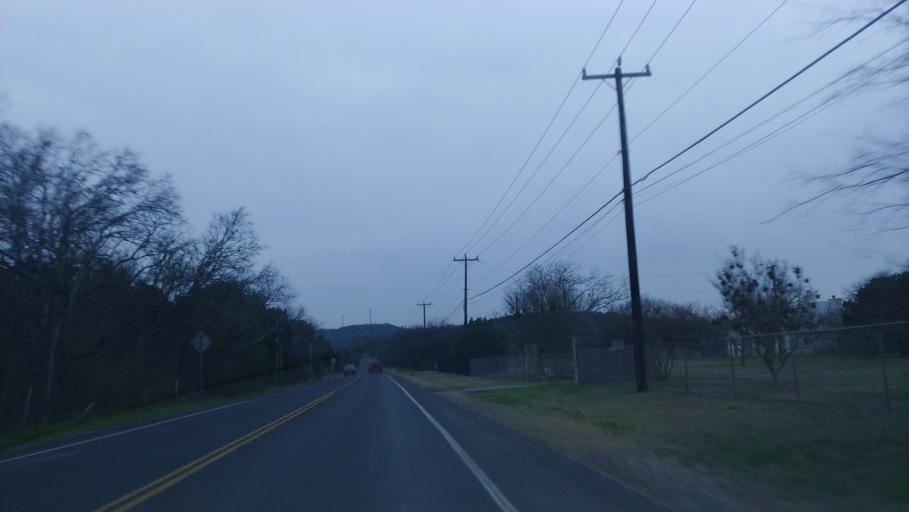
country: US
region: Texas
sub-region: Bexar County
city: Helotes
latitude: 29.6004
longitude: -98.6865
